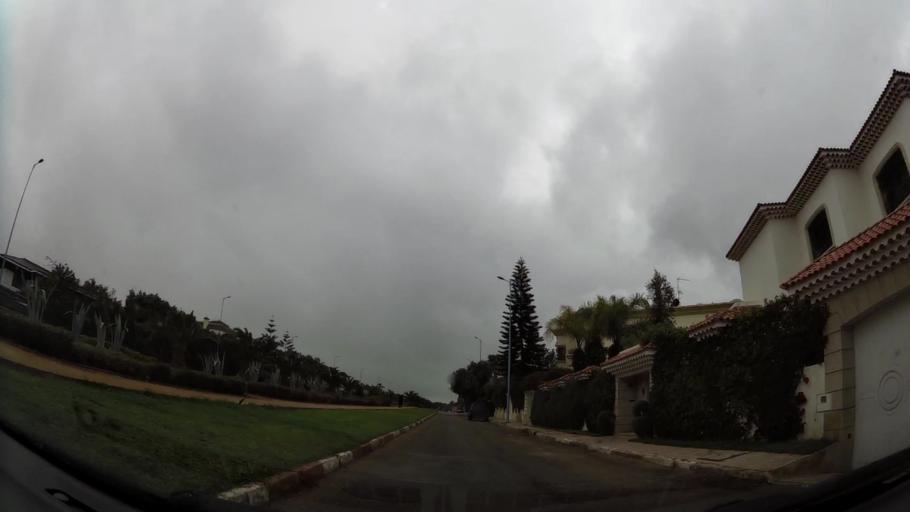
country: MA
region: Grand Casablanca
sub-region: Casablanca
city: Casablanca
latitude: 33.5385
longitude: -7.6265
